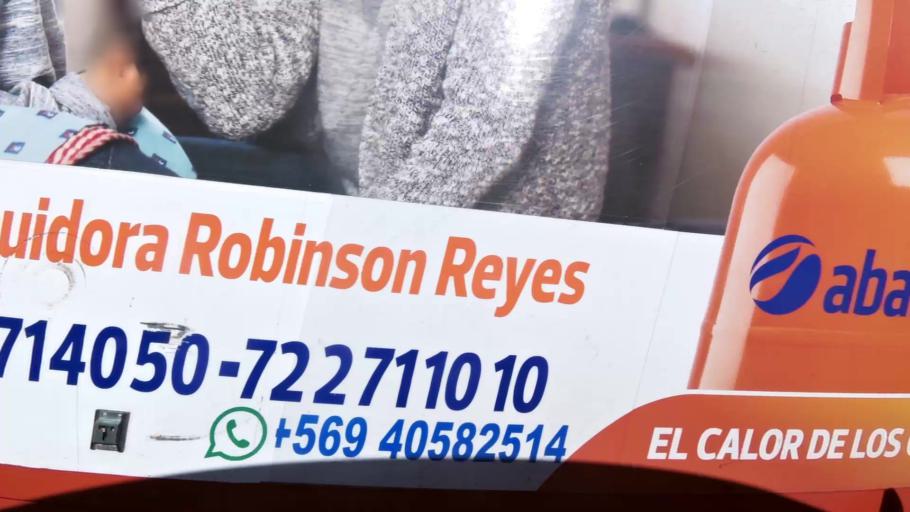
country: CL
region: O'Higgins
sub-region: Provincia de Colchagua
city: Chimbarongo
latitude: -34.5925
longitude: -70.9853
